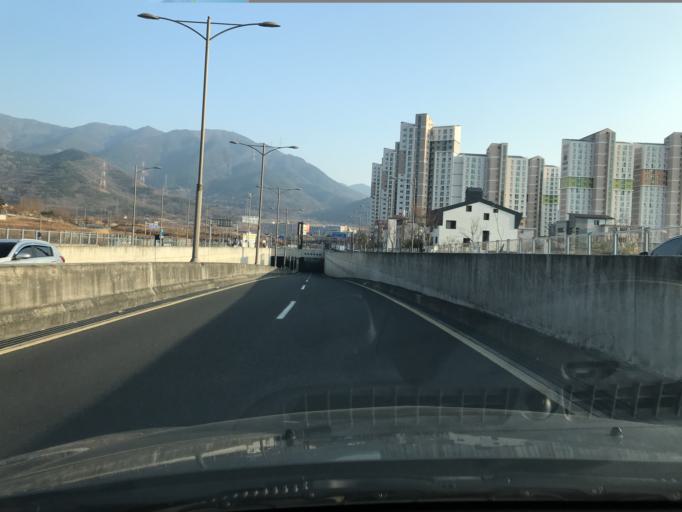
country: KR
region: Daegu
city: Hwawon
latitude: 35.7027
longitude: 128.4664
